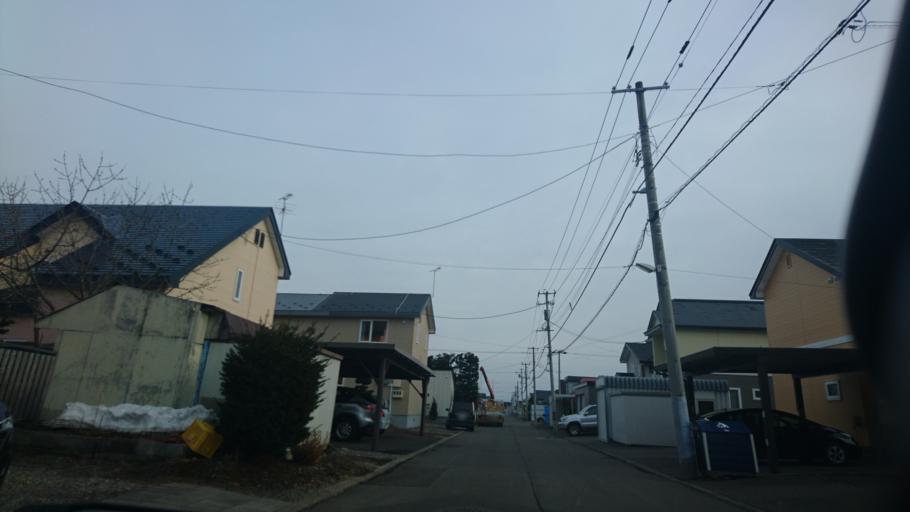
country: JP
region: Hokkaido
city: Otofuke
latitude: 43.0006
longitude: 143.1902
